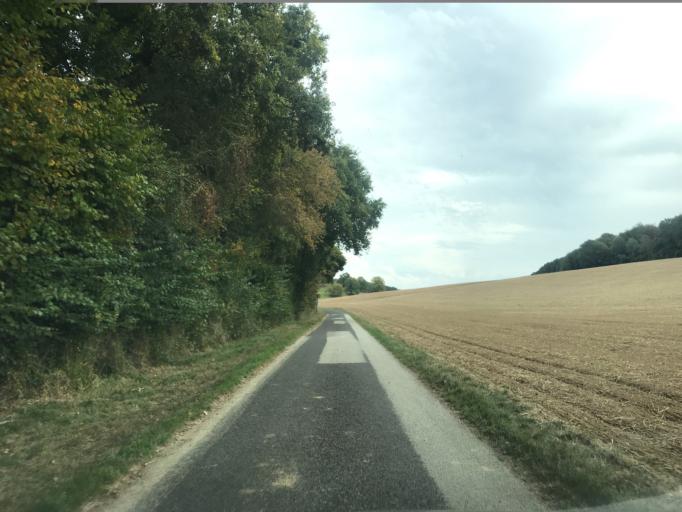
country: FR
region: Haute-Normandie
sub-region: Departement de l'Eure
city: Heudreville-sur-Eure
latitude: 49.0945
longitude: 1.2234
